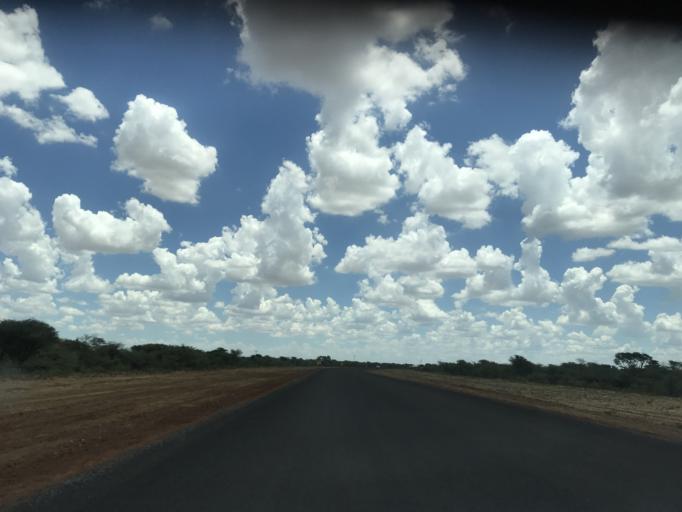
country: BW
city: Mabuli
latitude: -25.8054
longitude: 24.6801
